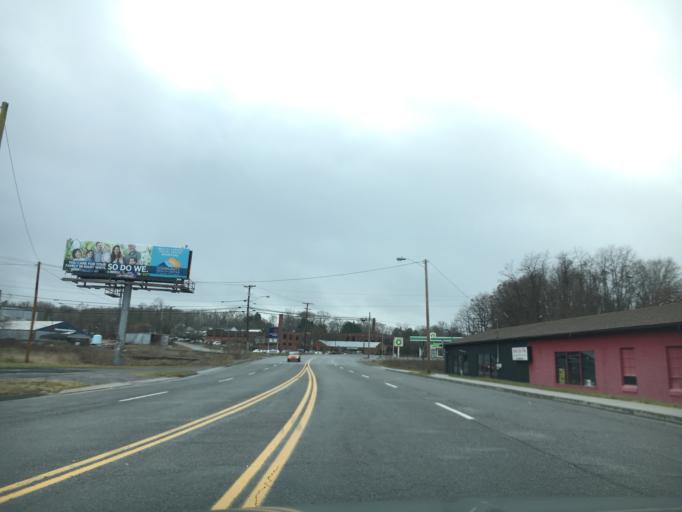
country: US
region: Virginia
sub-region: Montgomery County
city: Christiansburg
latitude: 37.1333
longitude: -80.3904
